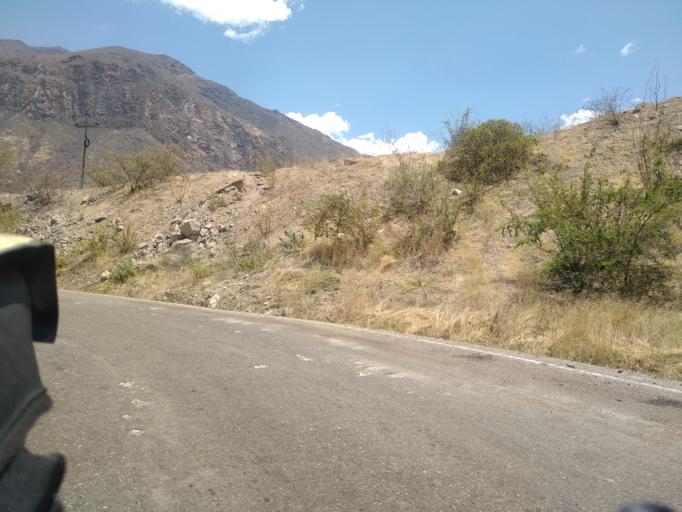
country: PE
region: Amazonas
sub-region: Provincia de Chachapoyas
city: Balsas
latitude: -6.8471
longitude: -78.0395
